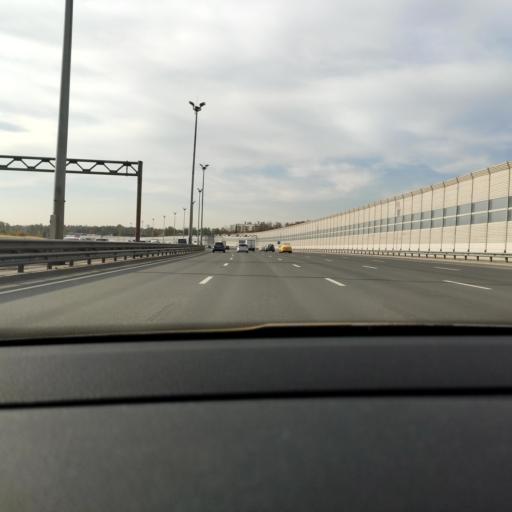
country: RU
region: Moskovskaya
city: Bolshevo
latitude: 55.9504
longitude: 37.8206
